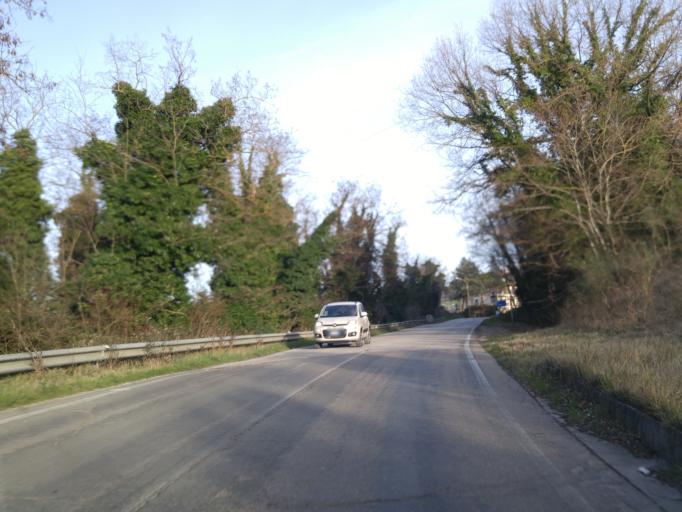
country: IT
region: The Marches
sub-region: Provincia di Pesaro e Urbino
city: Sant'Ippolito
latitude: 43.6883
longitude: 12.8531
